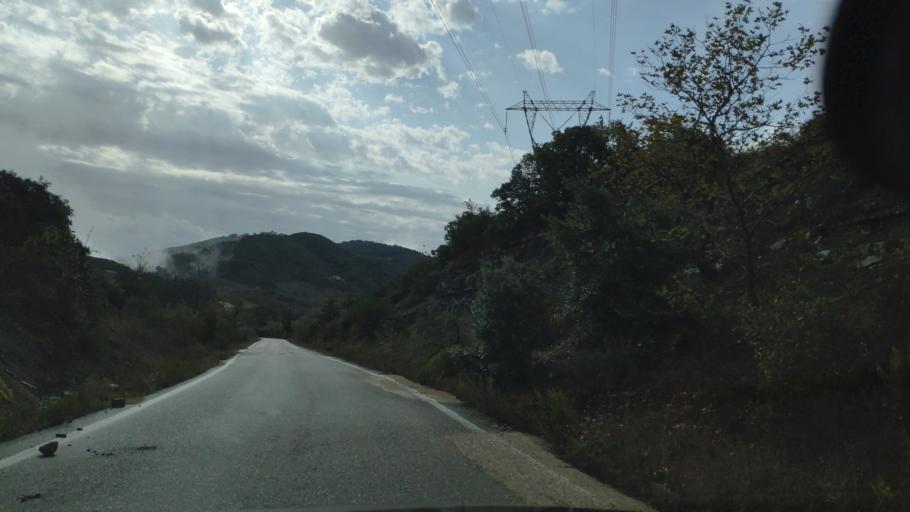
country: GR
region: West Greece
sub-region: Nomos Aitolias kai Akarnanias
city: Sardinia
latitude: 38.8746
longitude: 21.2737
